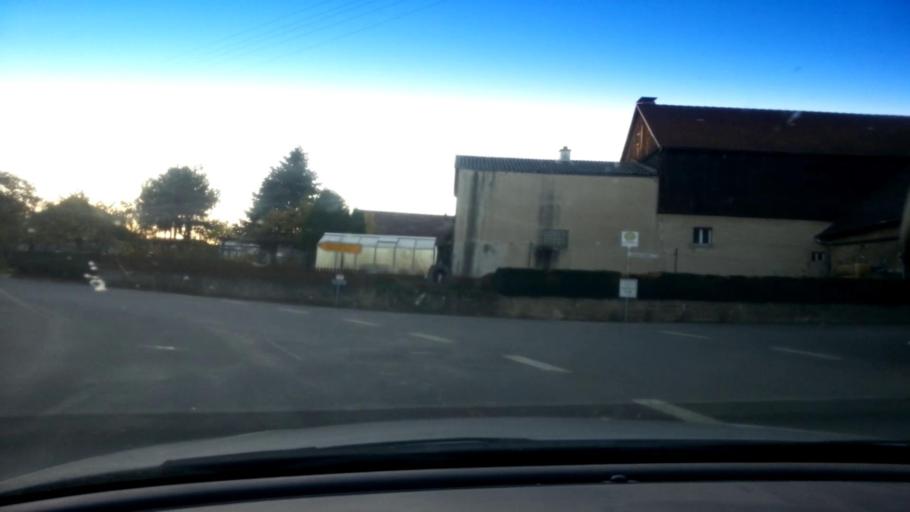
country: DE
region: Bavaria
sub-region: Upper Franconia
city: Heiligenstadt
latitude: 49.8560
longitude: 11.1160
